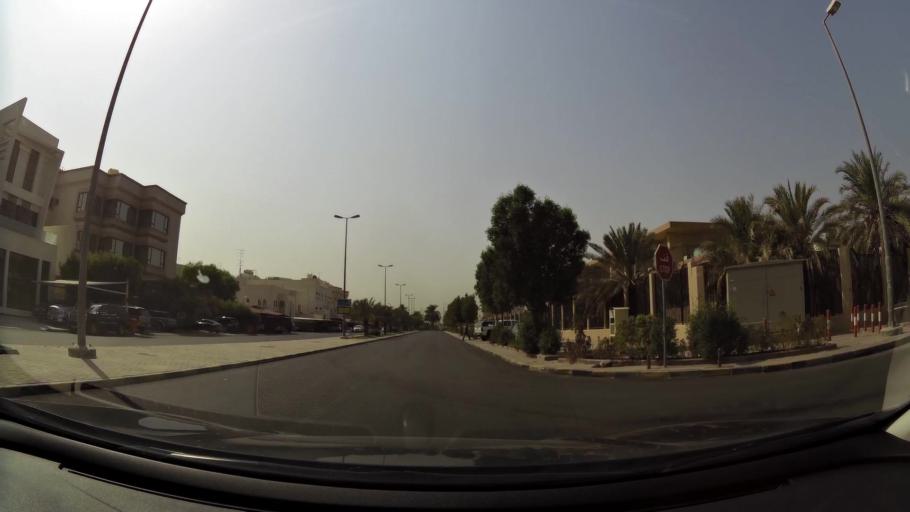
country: KW
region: Al Asimah
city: Ad Dasmah
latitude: 29.3474
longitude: 48.0037
